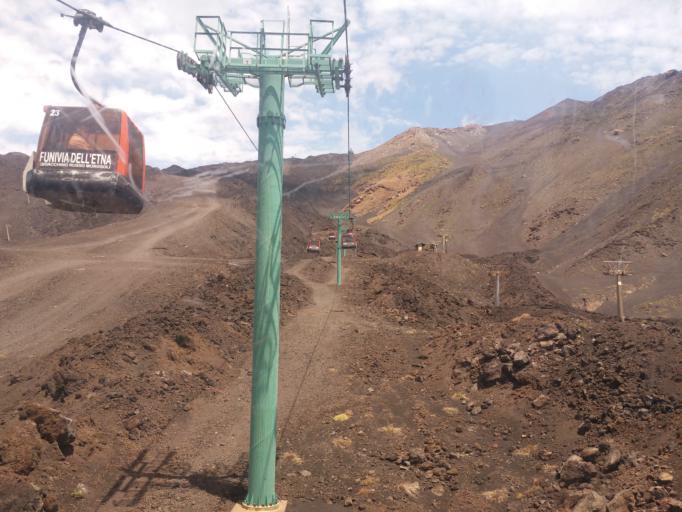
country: IT
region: Sicily
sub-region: Catania
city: Ragalna
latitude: 37.7064
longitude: 14.9993
